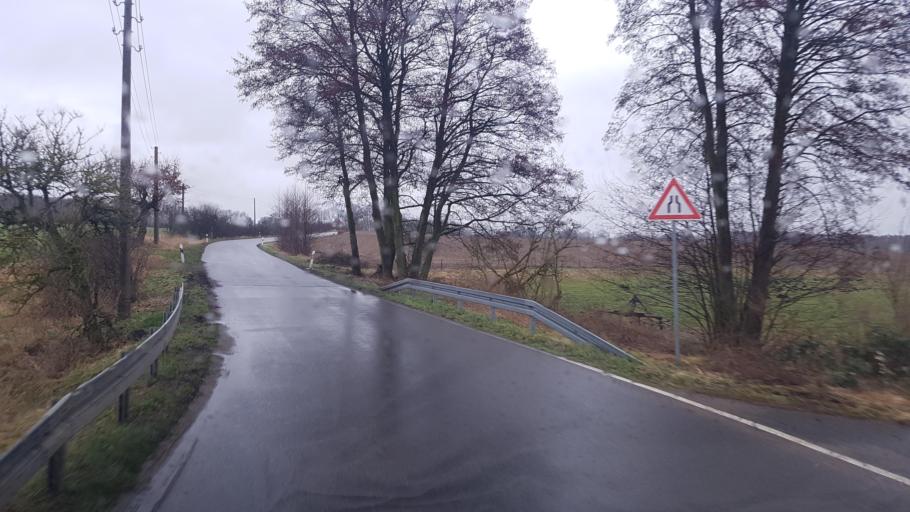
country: DE
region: Brandenburg
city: Oranienburg
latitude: 52.8815
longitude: 13.2116
